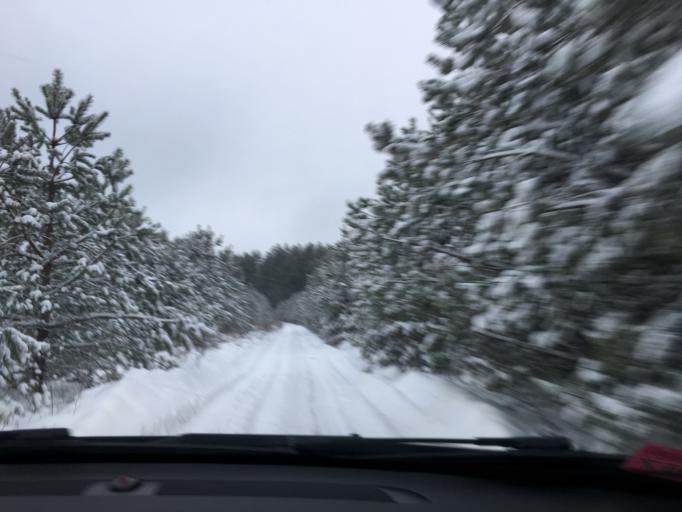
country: LT
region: Alytaus apskritis
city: Druskininkai
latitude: 53.9205
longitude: 24.1938
